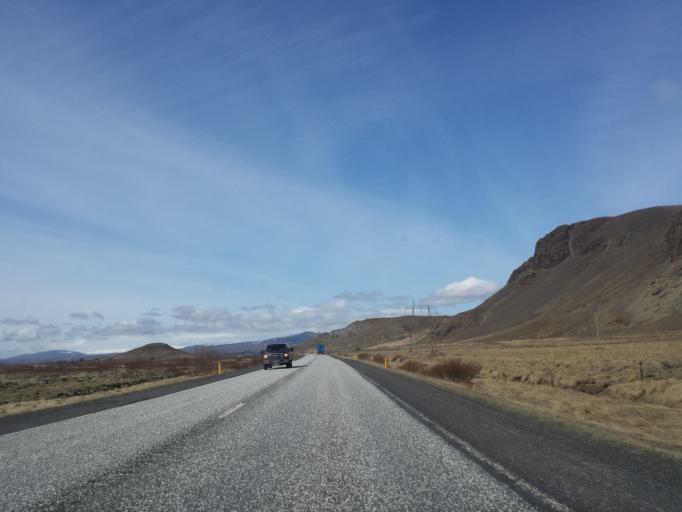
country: IS
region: South
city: Selfoss
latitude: 63.9552
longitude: -21.0460
